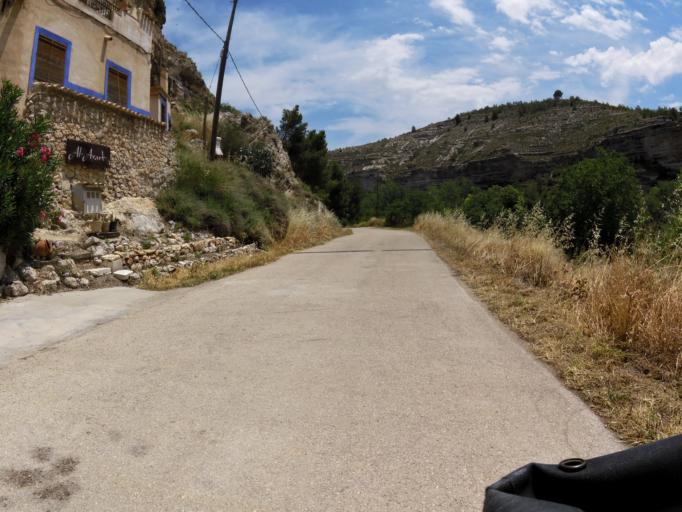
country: ES
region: Castille-La Mancha
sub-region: Provincia de Albacete
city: Casas de Juan Nunez
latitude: 39.1559
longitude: -1.5846
